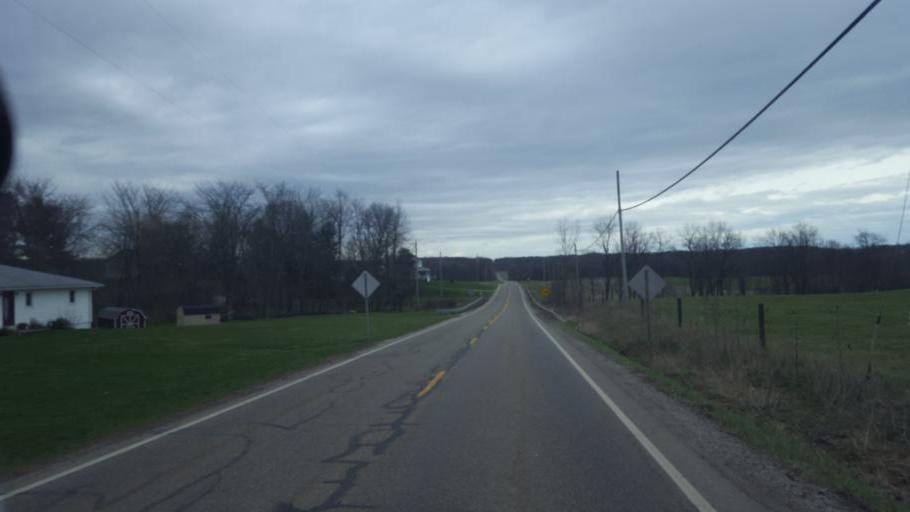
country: US
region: Ohio
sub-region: Richland County
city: Lexington
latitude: 40.6247
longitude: -82.6631
